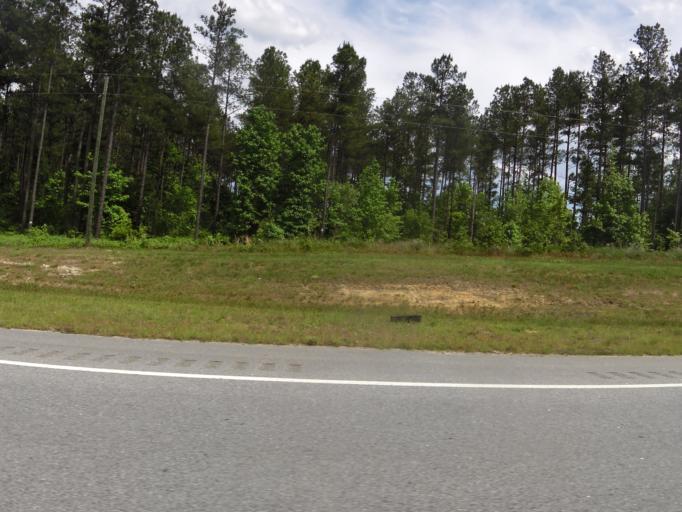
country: US
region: Georgia
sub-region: Jefferson County
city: Wadley
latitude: 32.7671
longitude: -82.3836
